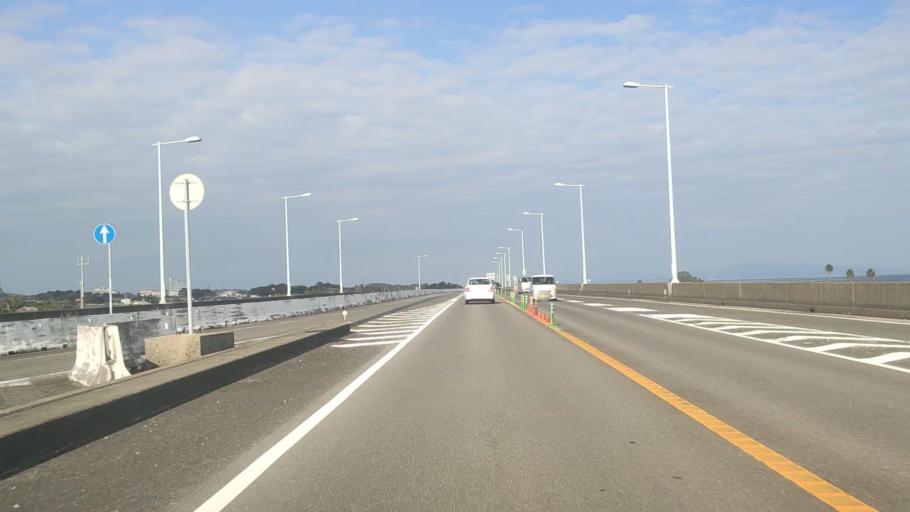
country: JP
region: Nagasaki
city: Shimabara
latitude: 32.7469
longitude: 130.3731
